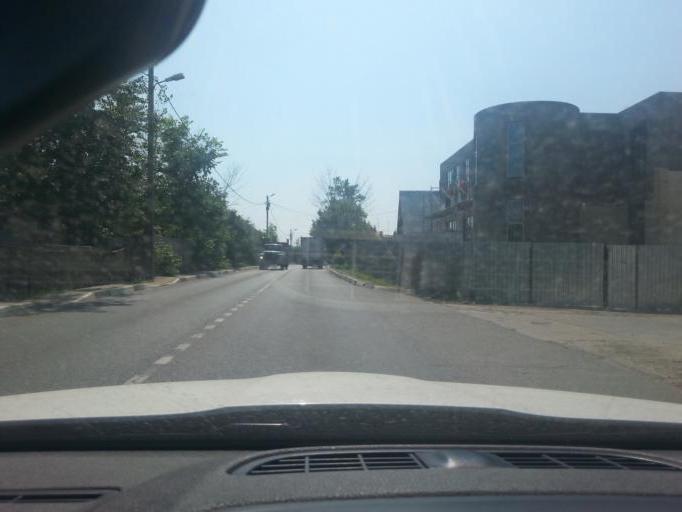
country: RU
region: Moskovskaya
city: Zheleznodorozhnyy
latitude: 55.7286
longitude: 38.0165
